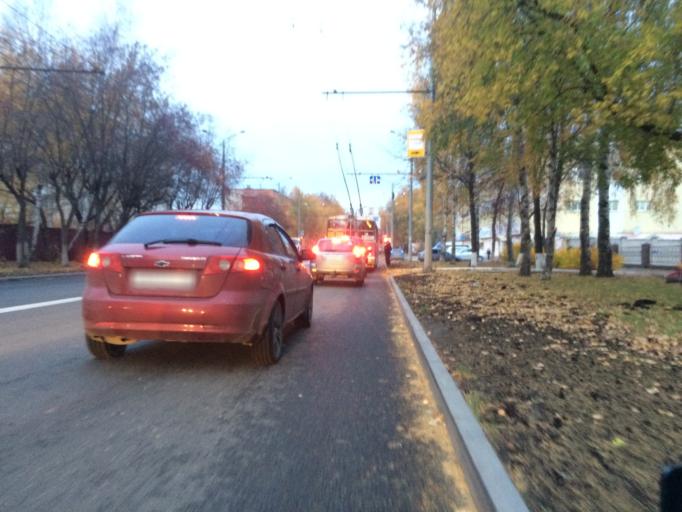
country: RU
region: Mariy-El
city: Yoshkar-Ola
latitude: 56.6154
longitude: 47.8832
